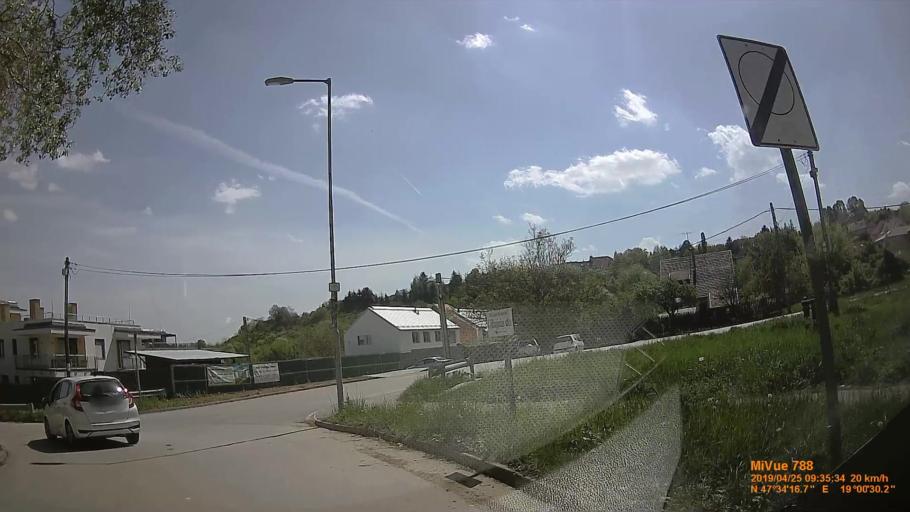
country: HU
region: Pest
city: Urom
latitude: 47.5713
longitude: 19.0085
